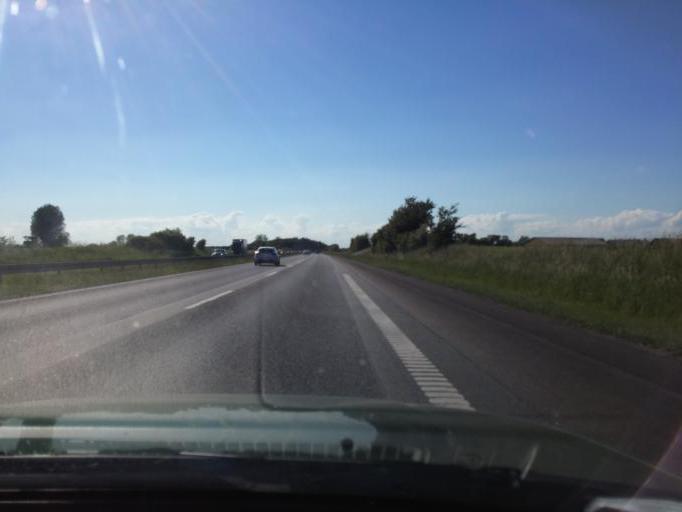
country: DK
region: South Denmark
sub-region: Middelfart Kommune
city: Ejby
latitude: 55.4625
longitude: 9.9165
